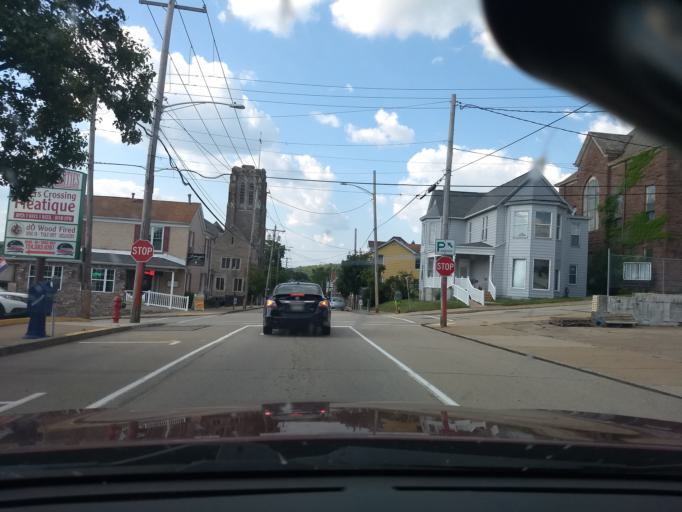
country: US
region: Pennsylvania
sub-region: Westmoreland County
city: Irwin
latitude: 40.3314
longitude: -79.7098
